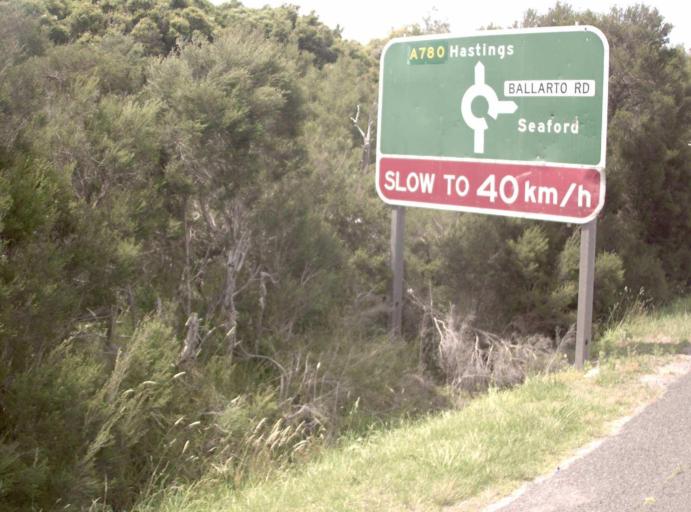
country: AU
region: Victoria
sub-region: Casey
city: Cranbourne South
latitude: -38.1194
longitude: 145.2312
